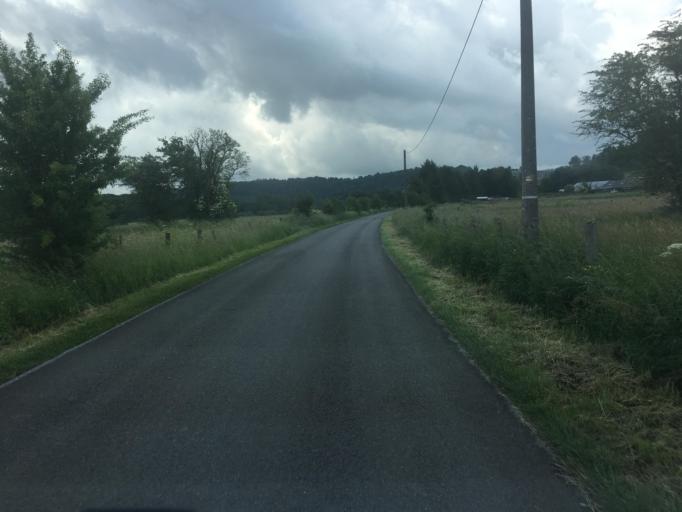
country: BE
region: Wallonia
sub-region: Province du Luxembourg
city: Florenville
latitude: 49.7170
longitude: 5.2588
